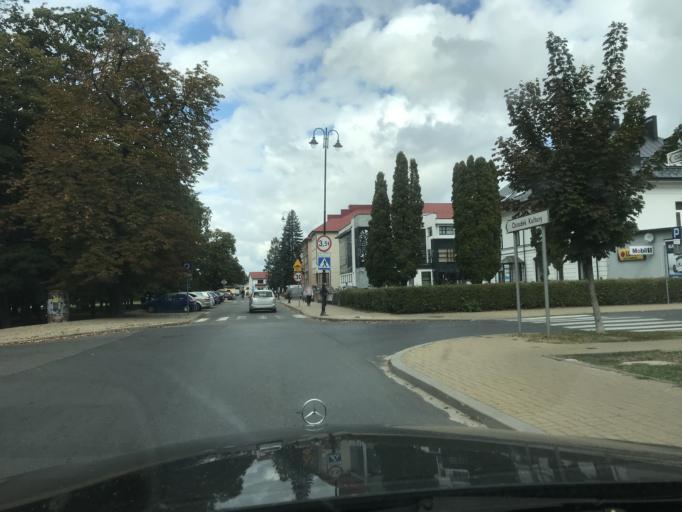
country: PL
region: Lublin Voivodeship
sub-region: Powiat janowski
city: Janow Lubelski
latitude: 50.7043
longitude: 22.4176
